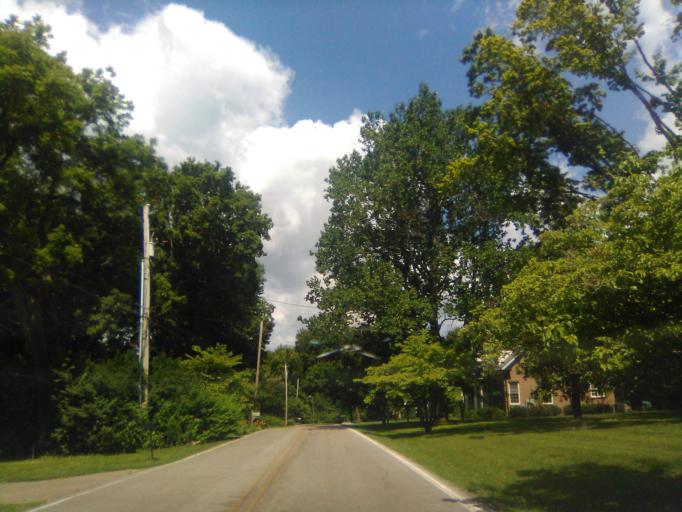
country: US
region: Tennessee
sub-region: Davidson County
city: Belle Meade
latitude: 36.1051
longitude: -86.8612
